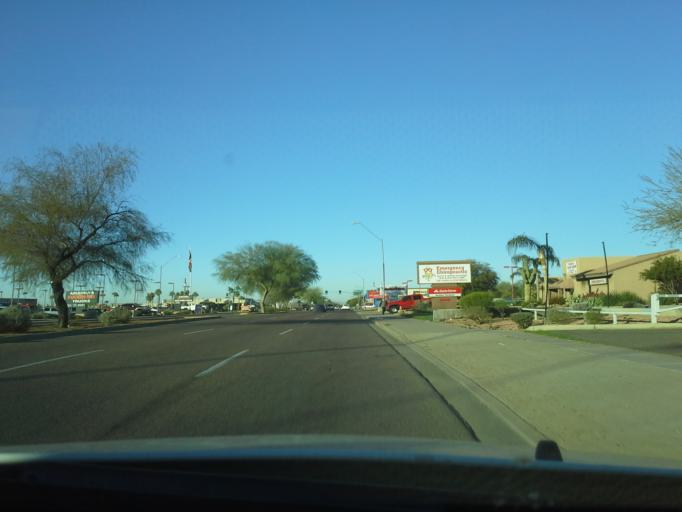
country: US
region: Arizona
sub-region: Maricopa County
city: Paradise Valley
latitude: 33.6406
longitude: -112.0374
